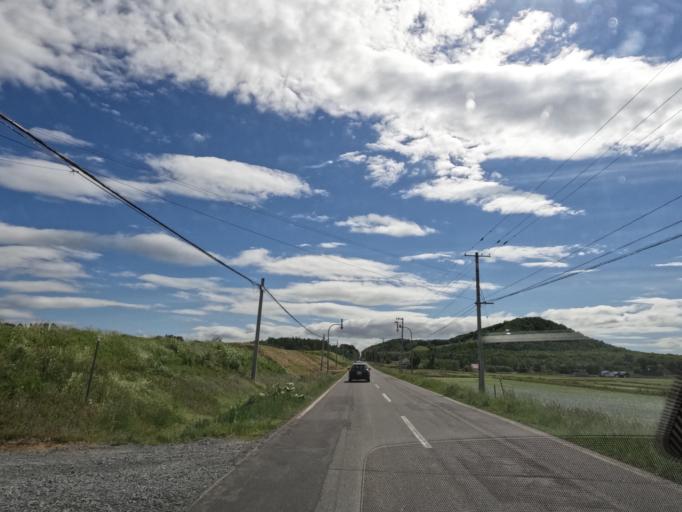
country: JP
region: Hokkaido
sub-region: Asahikawa-shi
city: Asahikawa
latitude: 43.8418
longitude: 142.5475
